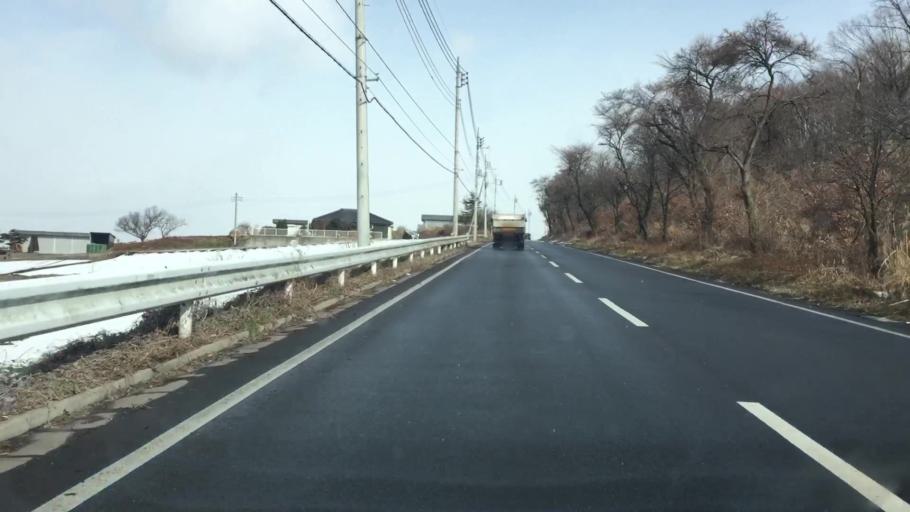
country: JP
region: Gunma
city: Numata
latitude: 36.6120
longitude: 139.0794
